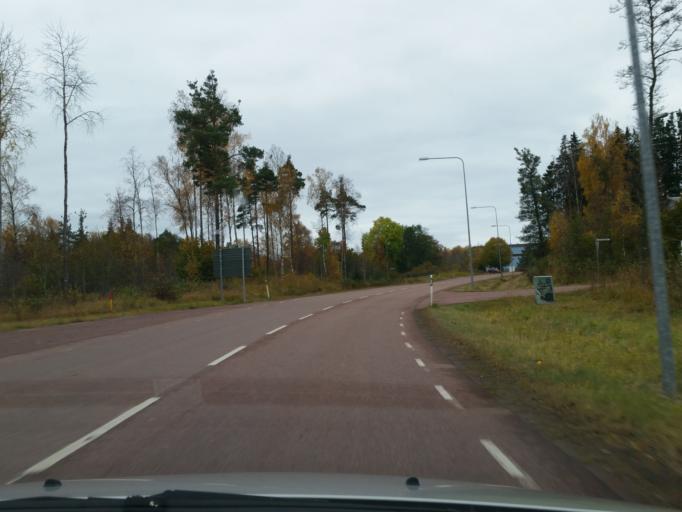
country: AX
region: Mariehamns stad
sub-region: Mariehamn
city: Mariehamn
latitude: 60.1114
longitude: 19.9140
